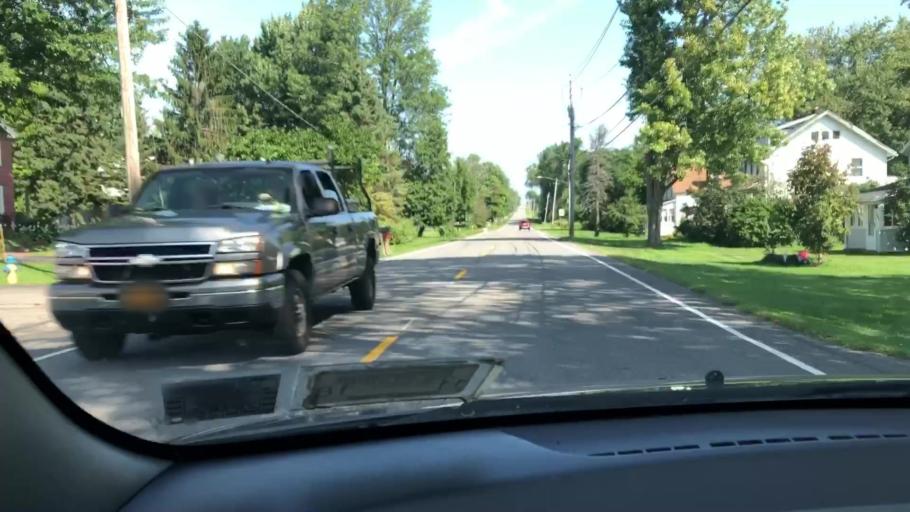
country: US
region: New York
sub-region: Wayne County
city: Macedon
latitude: 43.0962
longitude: -77.3206
